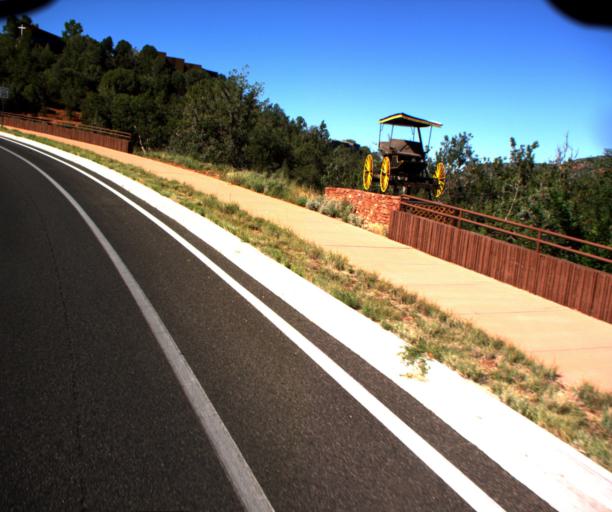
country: US
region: Arizona
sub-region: Coconino County
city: Sedona
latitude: 34.8517
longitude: -111.7655
